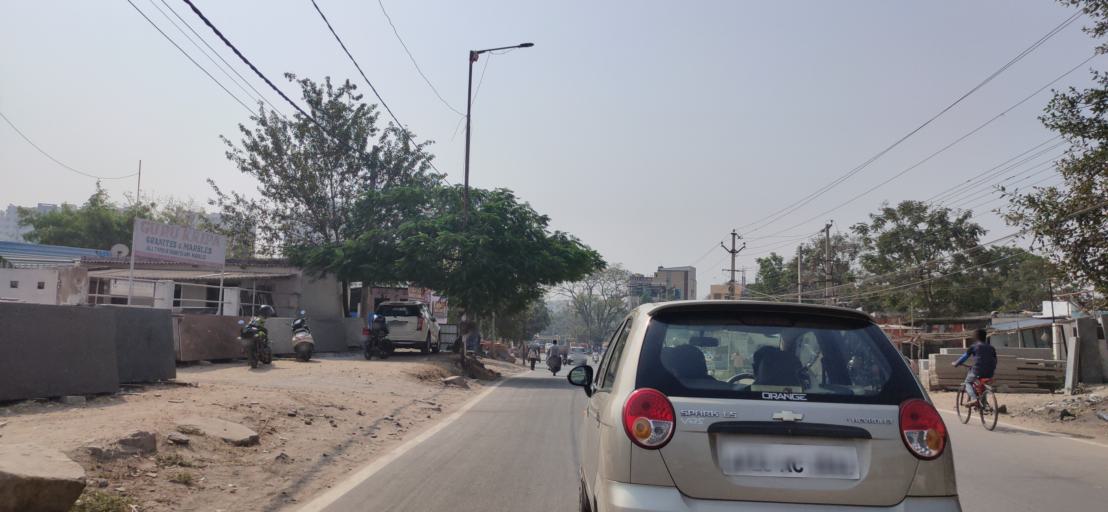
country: IN
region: Telangana
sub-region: Rangareddi
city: Kukatpalli
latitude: 17.5047
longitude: 78.4079
